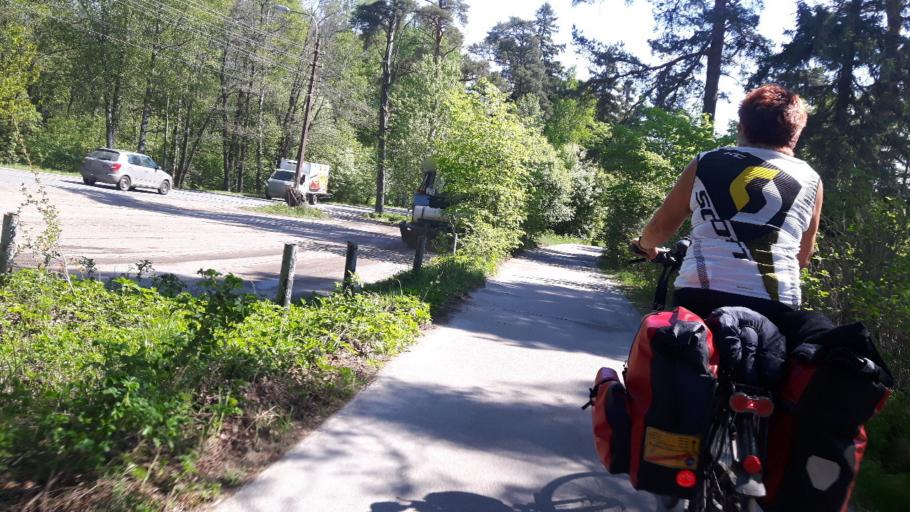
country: RU
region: St.-Petersburg
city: Komarovo
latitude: 60.1764
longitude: 29.7950
